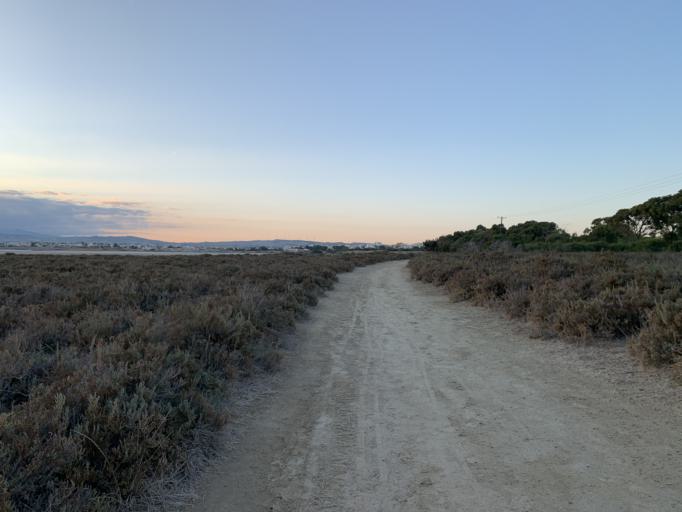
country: CY
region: Larnaka
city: Larnaca
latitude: 34.9037
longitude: 33.6233
